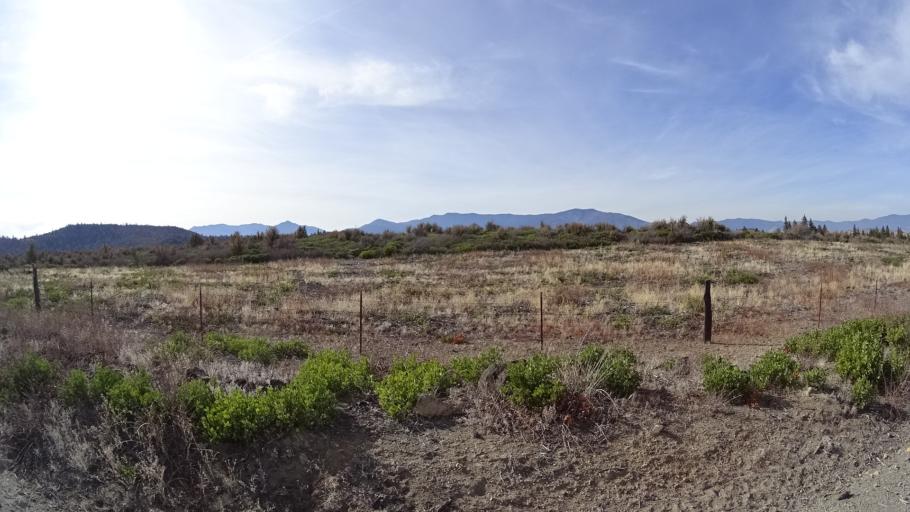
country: US
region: California
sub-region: Siskiyou County
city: Weed
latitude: 41.4867
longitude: -122.3681
